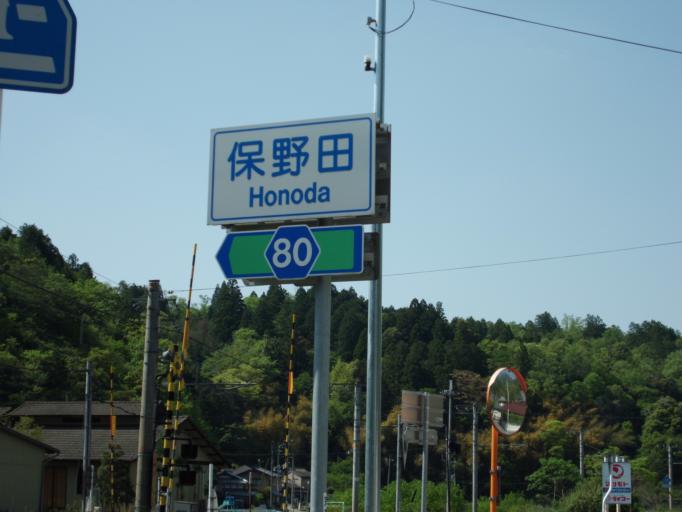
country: JP
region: Kyoto
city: Kameoka
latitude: 35.1658
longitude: 135.4980
